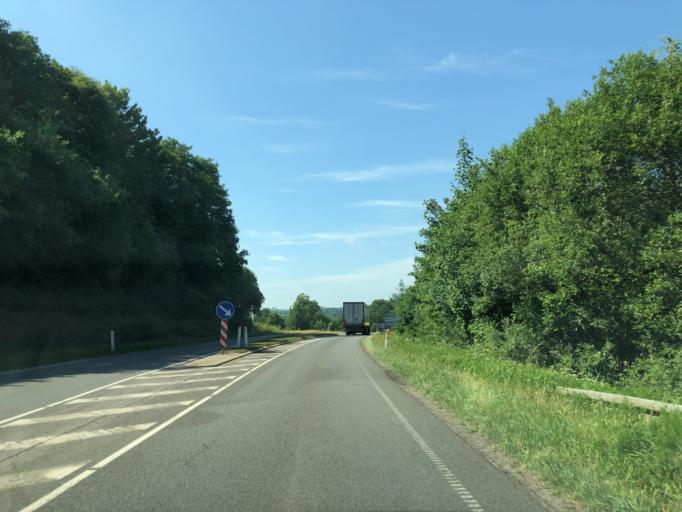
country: DK
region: South Denmark
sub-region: Vejle Kommune
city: Jelling
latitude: 55.6740
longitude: 9.3856
